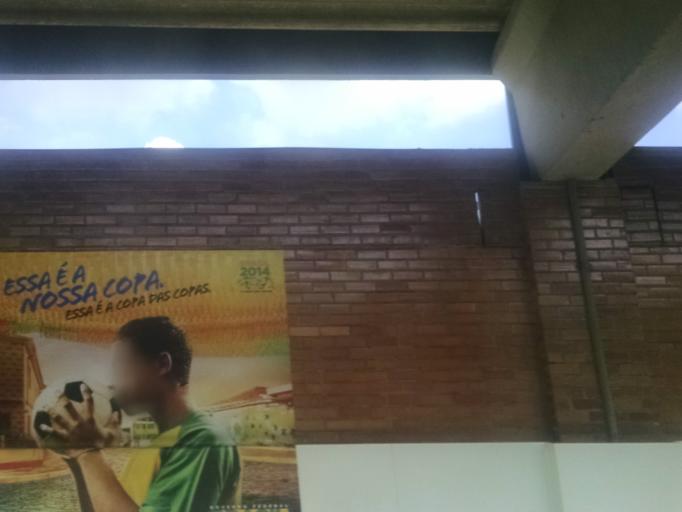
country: BR
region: Rio de Janeiro
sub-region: Rio De Janeiro
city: Rio de Janeiro
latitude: -22.8785
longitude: -43.2735
